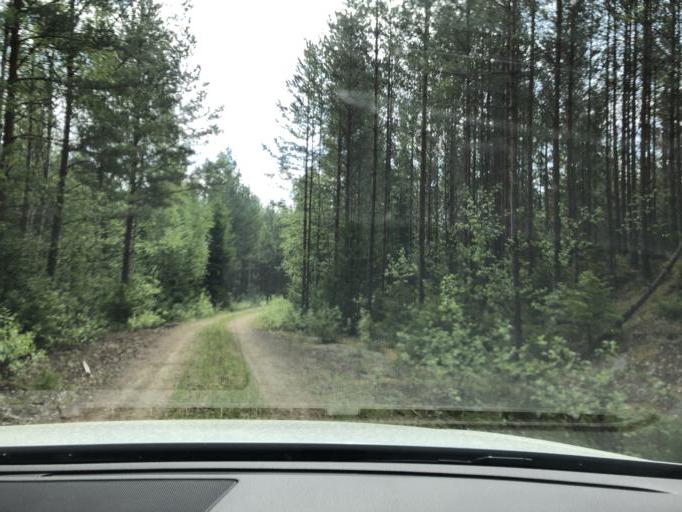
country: SE
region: Dalarna
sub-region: Avesta Kommun
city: Horndal
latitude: 60.2230
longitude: 16.5148
